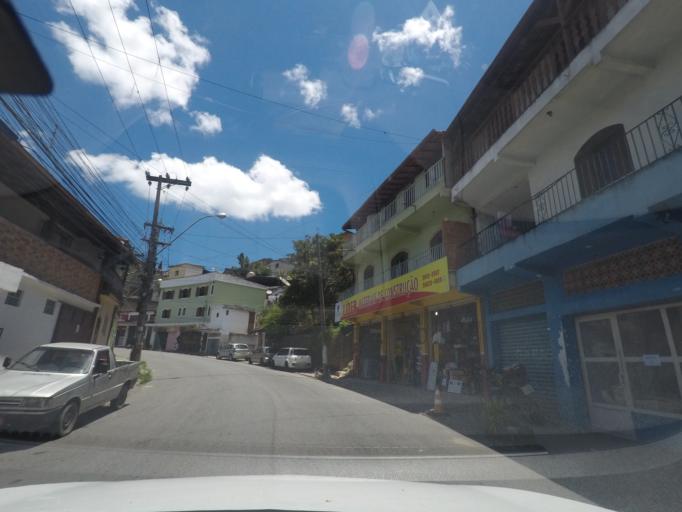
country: BR
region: Rio de Janeiro
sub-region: Teresopolis
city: Teresopolis
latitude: -22.4308
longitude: -42.9689
